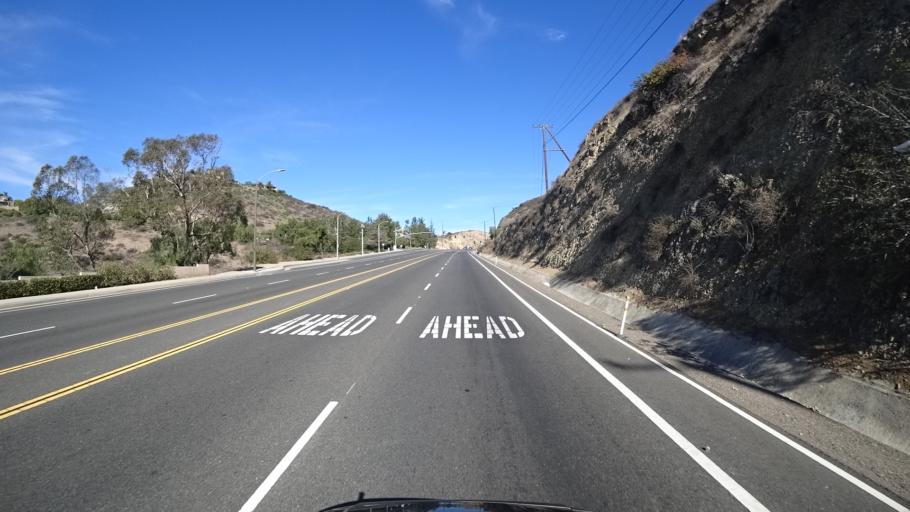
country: US
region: California
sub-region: Orange County
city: North Tustin
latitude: 33.7914
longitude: -117.7869
